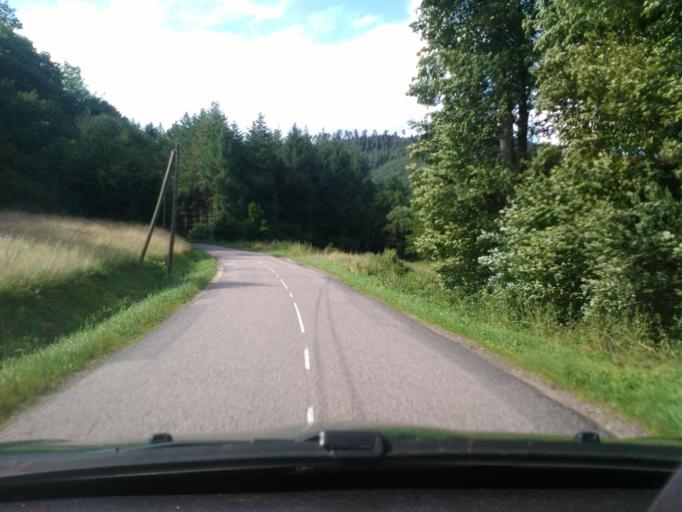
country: FR
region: Lorraine
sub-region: Departement des Vosges
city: Bruyeres
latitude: 48.2278
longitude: 6.7634
